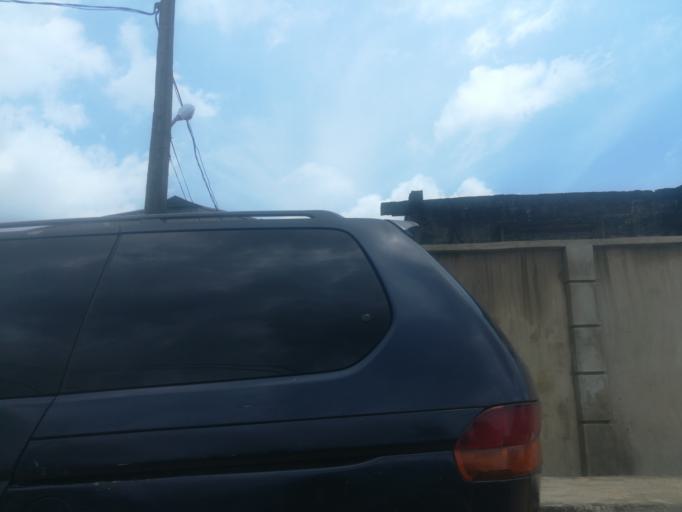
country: NG
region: Lagos
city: Ojota
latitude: 6.5646
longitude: 3.3912
